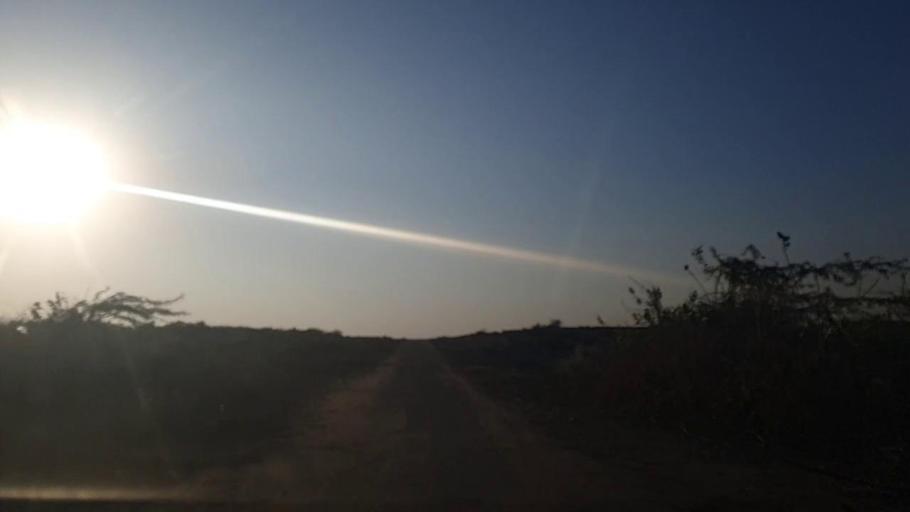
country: PK
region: Sindh
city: Jam Sahib
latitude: 26.3488
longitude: 68.6706
